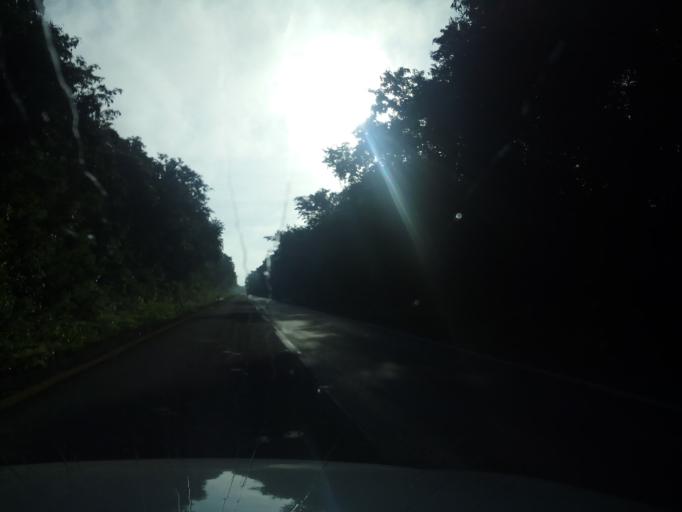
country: MX
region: Yucatan
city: Tunkas
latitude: 20.7663
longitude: -88.8080
